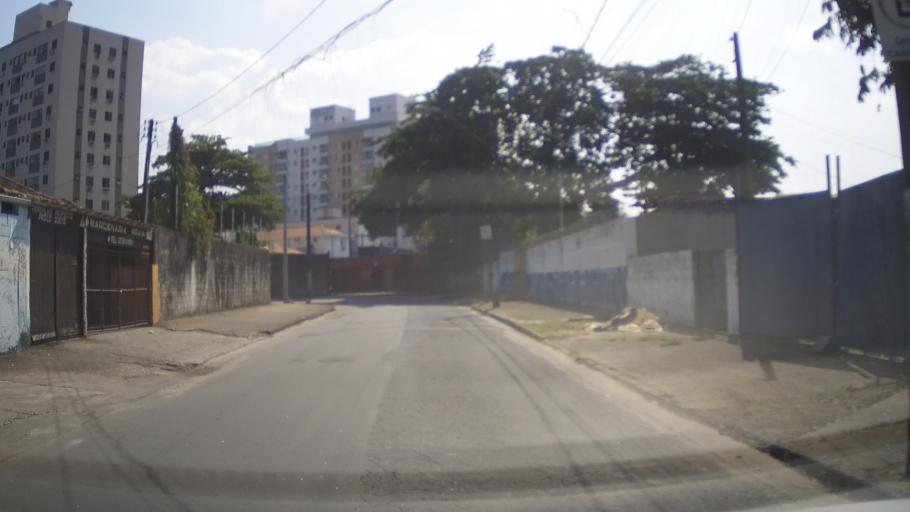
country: BR
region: Sao Paulo
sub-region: Santos
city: Santos
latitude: -23.9705
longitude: -46.3000
